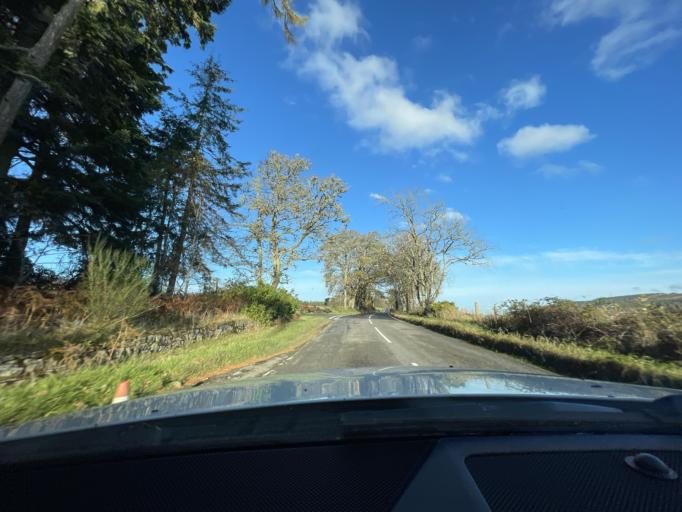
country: GB
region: Scotland
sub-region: Highland
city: Inverness
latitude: 57.4023
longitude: -4.3173
